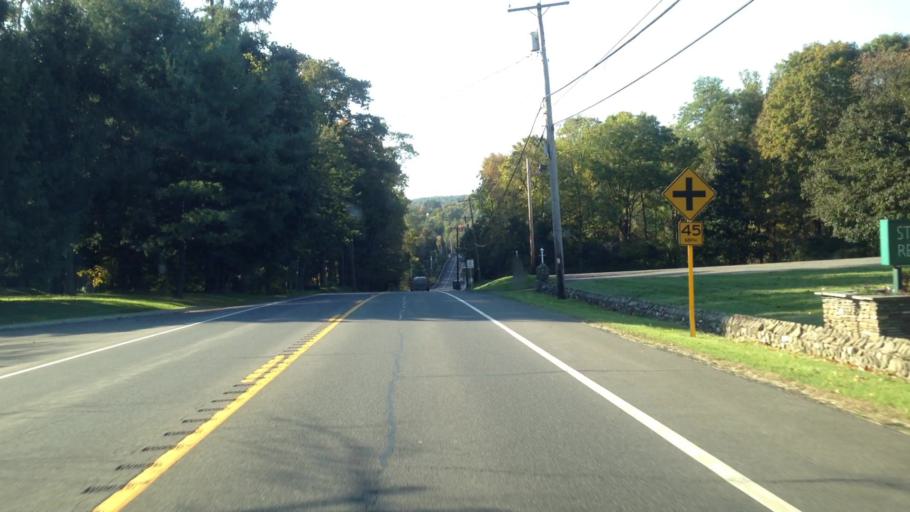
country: US
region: New York
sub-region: Dutchess County
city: Hyde Park
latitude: 41.7973
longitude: -73.9593
